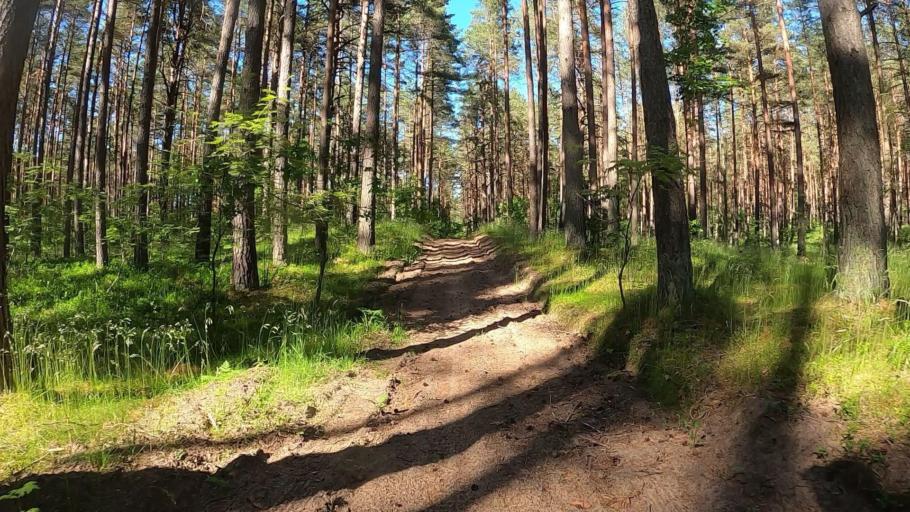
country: LV
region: Riga
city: Bergi
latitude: 57.0081
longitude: 24.2537
